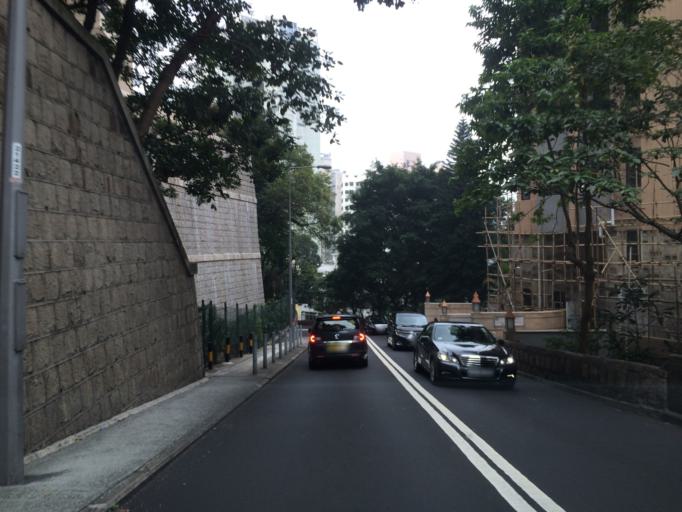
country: HK
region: Central and Western
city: Central
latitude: 22.2740
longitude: 114.1581
